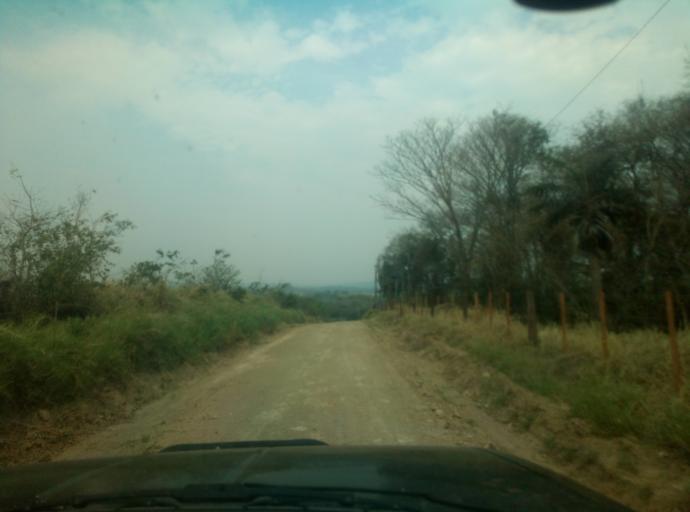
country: PY
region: Caaguazu
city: San Joaquin
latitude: -25.1027
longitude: -56.1316
